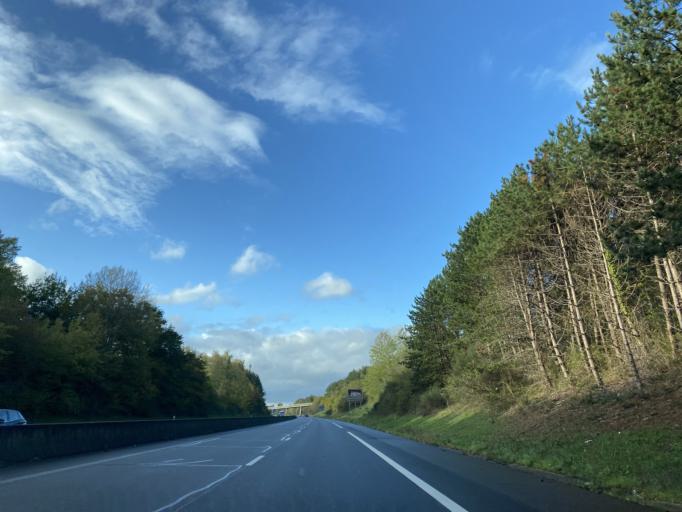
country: FR
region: Centre
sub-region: Departement du Cher
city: Vierzon
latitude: 47.2259
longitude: 2.1061
